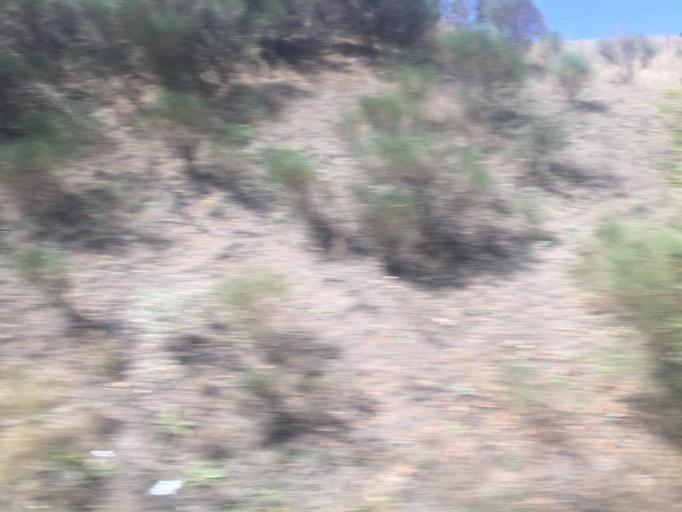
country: TR
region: Balikesir
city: Susurluk
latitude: 39.8817
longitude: 28.1653
